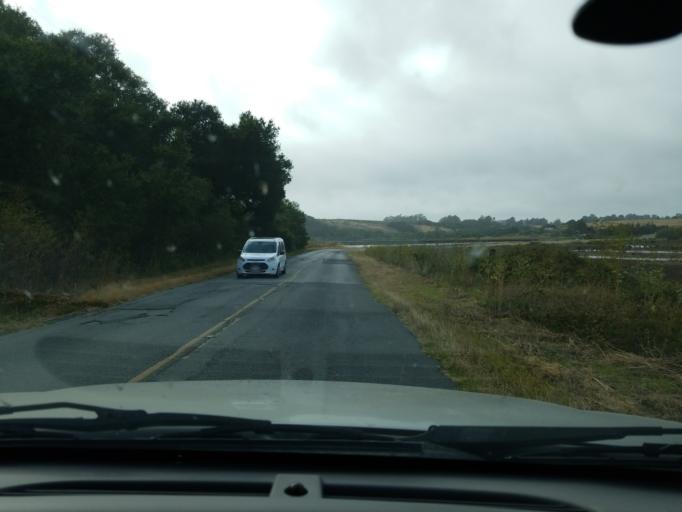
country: US
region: California
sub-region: Monterey County
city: Las Lomas
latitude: 36.8530
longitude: -121.7539
